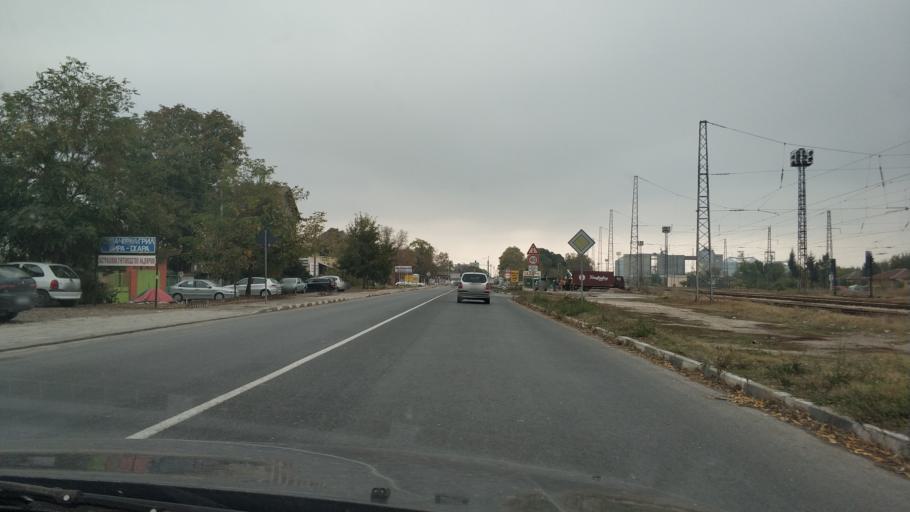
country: BG
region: Plovdiv
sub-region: Obshtina Plovdiv
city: Plovdiv
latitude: 42.2329
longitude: 24.7239
